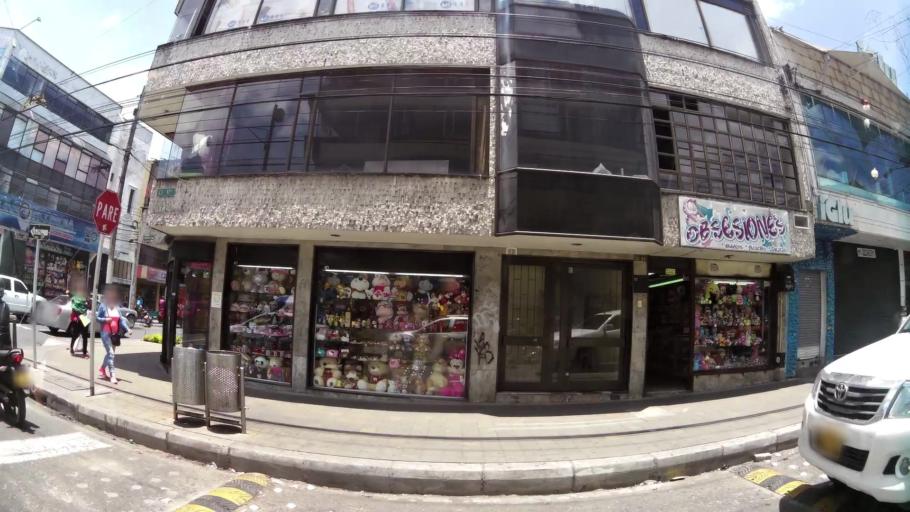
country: CO
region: Bogota D.C.
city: Bogota
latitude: 4.5849
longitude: -74.1001
